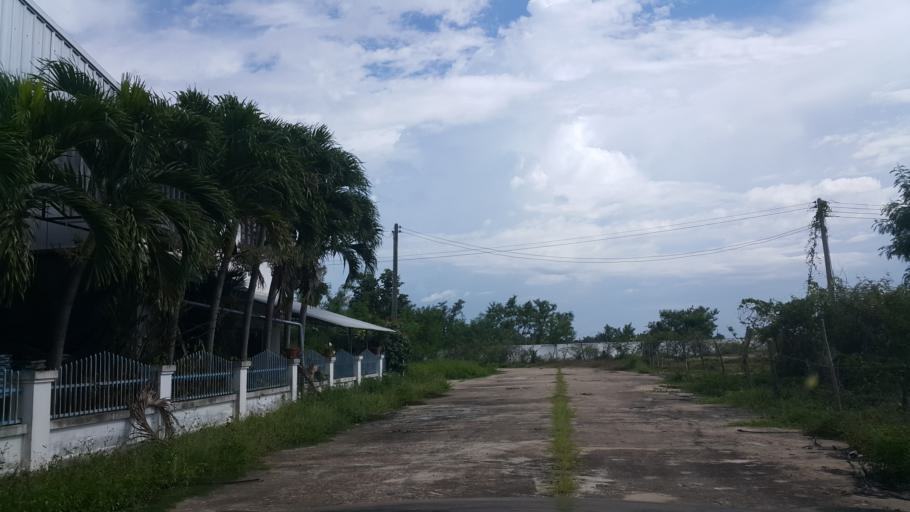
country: TH
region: Chiang Mai
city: San Kamphaeng
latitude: 18.7177
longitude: 99.1563
